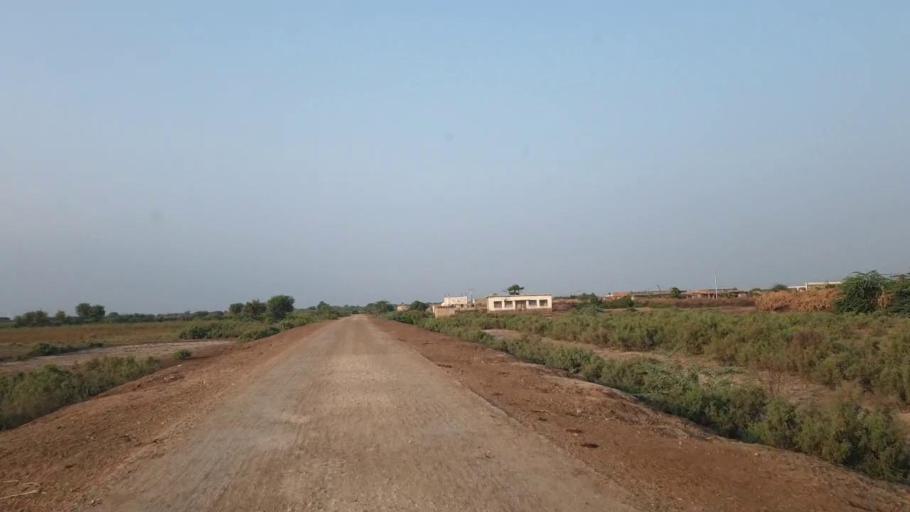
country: PK
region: Sindh
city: Tando Ghulam Ali
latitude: 25.0503
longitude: 68.9645
